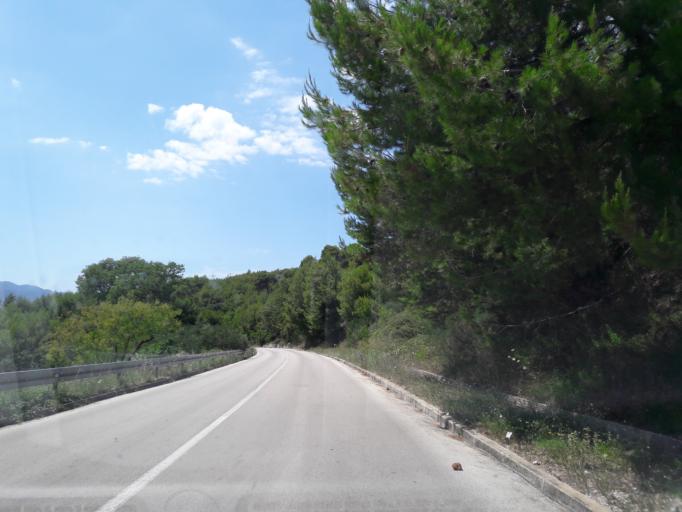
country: HR
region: Dubrovacko-Neretvanska
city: Korcula
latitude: 42.9826
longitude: 17.1144
